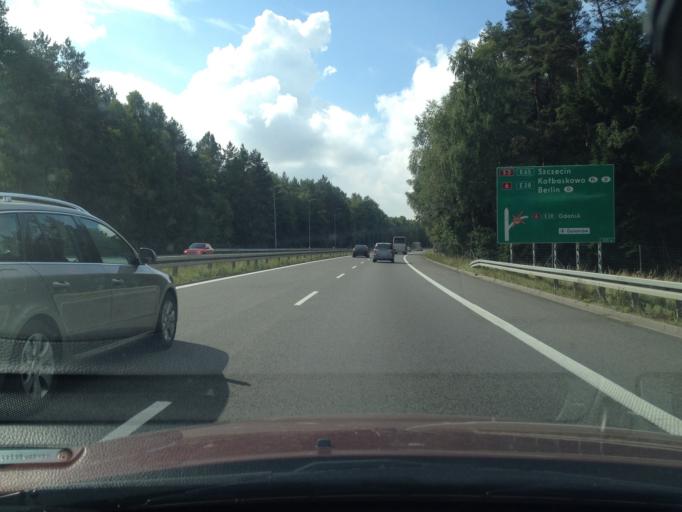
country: PL
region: West Pomeranian Voivodeship
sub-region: Powiat goleniowski
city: Goleniow
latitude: 53.5954
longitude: 14.8247
